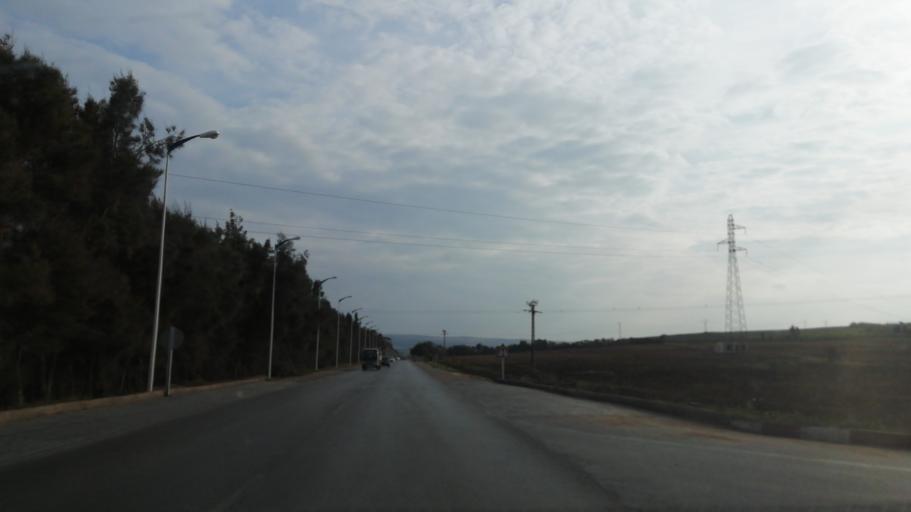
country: DZ
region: Mostaganem
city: Mostaganem
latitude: 35.8878
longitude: 0.0765
